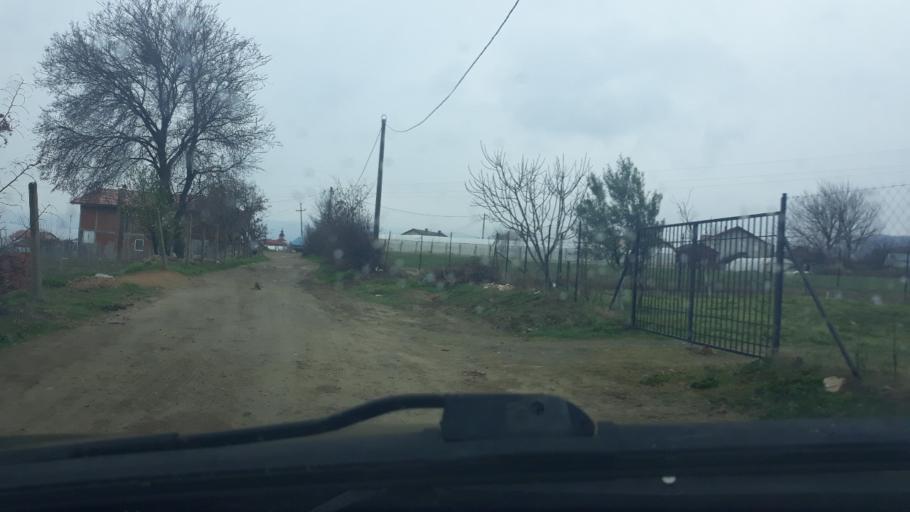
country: MK
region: Dojran
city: Star Dojran
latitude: 41.2644
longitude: 22.7506
